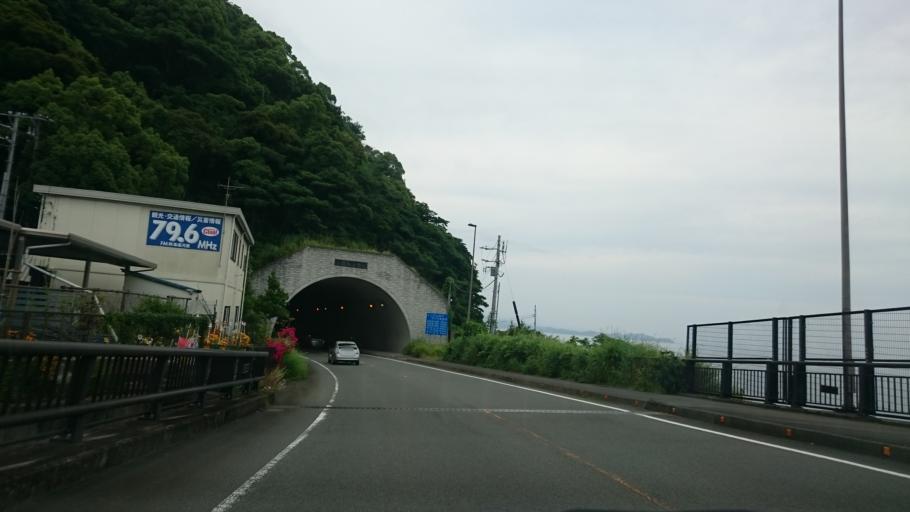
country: JP
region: Shizuoka
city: Atami
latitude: 35.0430
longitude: 139.0993
